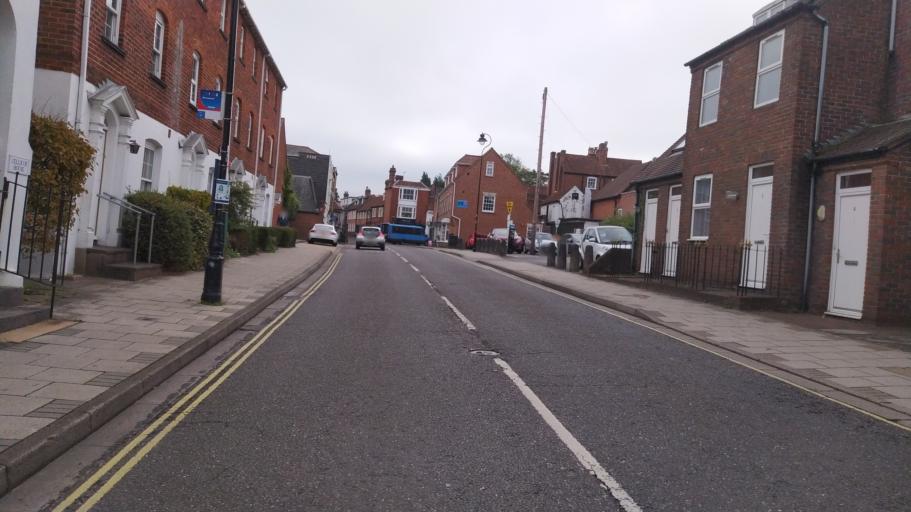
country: GB
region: England
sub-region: Hampshire
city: Lymington
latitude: 50.7600
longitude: -1.5388
